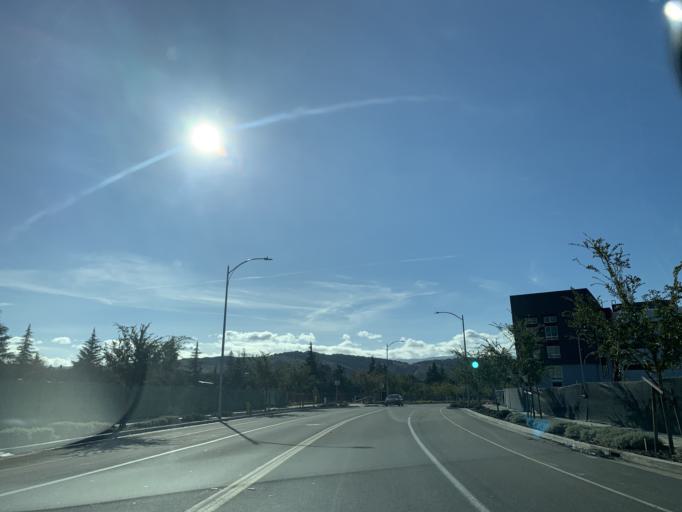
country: US
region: California
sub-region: Santa Clara County
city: Seven Trees
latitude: 37.2411
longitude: -121.7863
